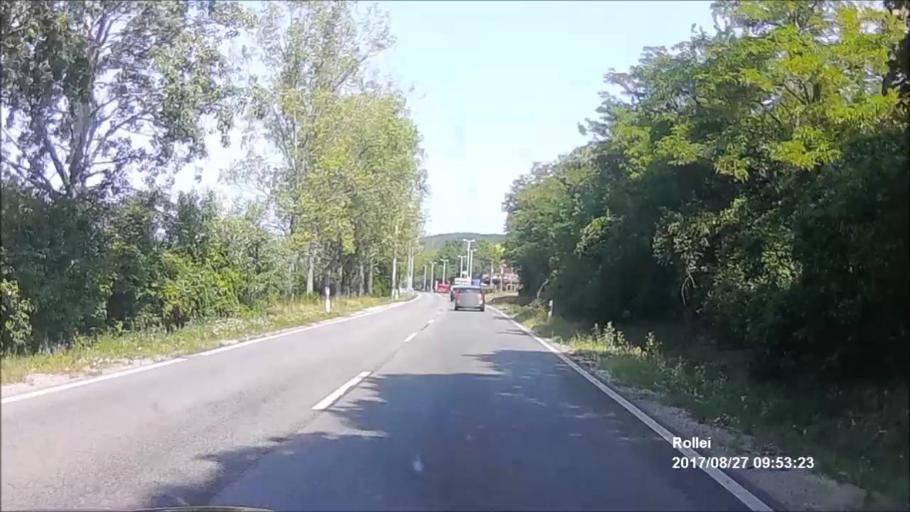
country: HU
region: Gyor-Moson-Sopron
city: Sopron
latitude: 47.7130
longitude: 16.5726
